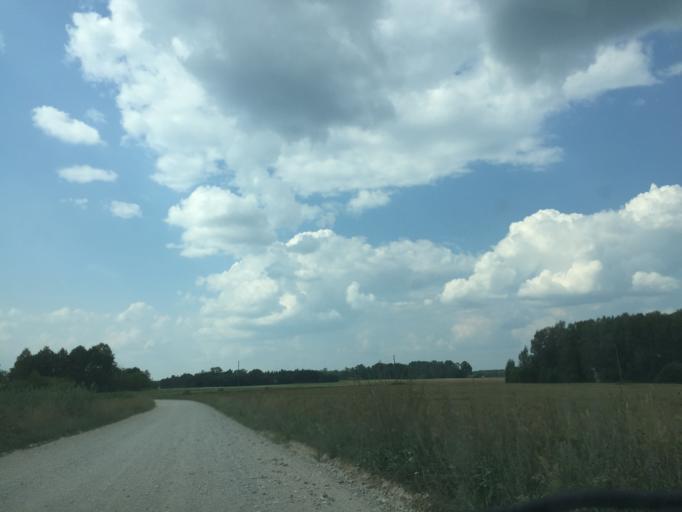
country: LV
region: Auces Novads
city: Auce
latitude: 56.4035
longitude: 23.0507
